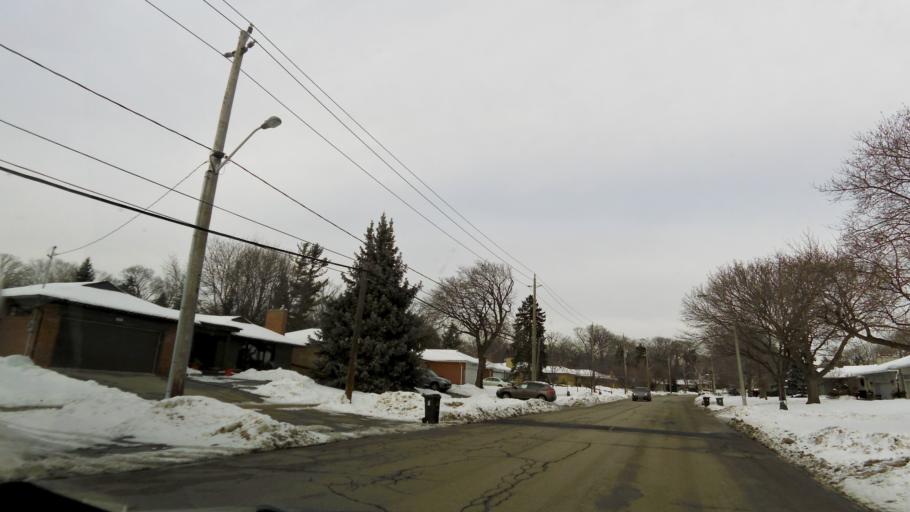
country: CA
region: Ontario
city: Etobicoke
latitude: 43.6681
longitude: -79.5515
